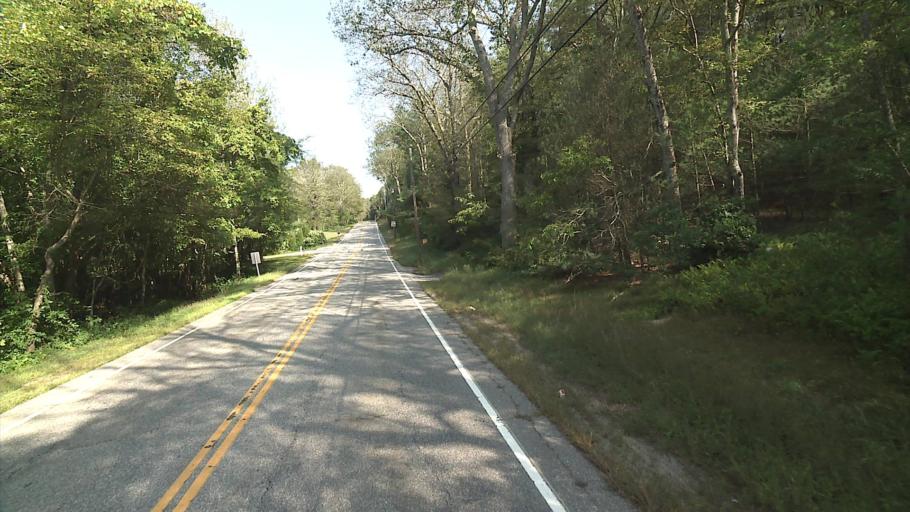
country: US
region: Connecticut
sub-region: Windham County
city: Plainfield Village
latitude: 41.6843
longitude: -71.9669
